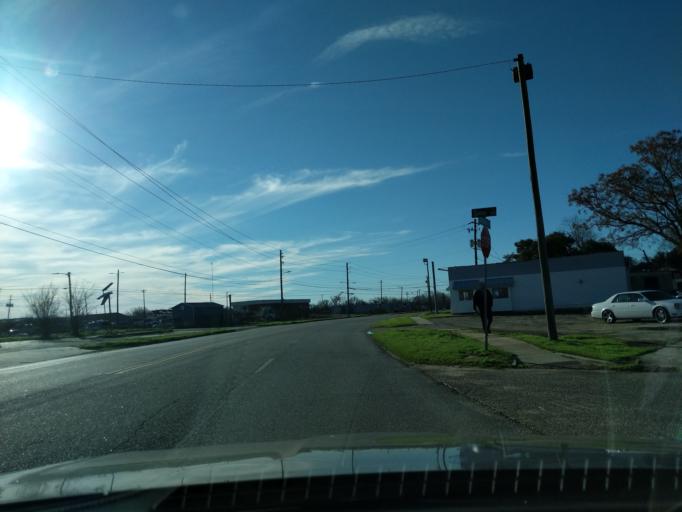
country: US
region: Georgia
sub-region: Richmond County
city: Augusta
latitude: 33.4575
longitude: -81.9547
